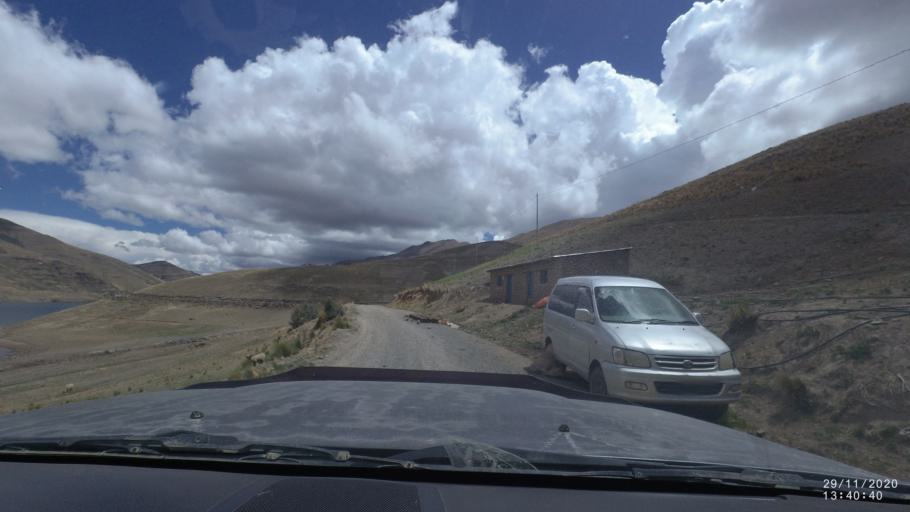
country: BO
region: Cochabamba
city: Cochabamba
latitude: -17.1294
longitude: -66.3262
